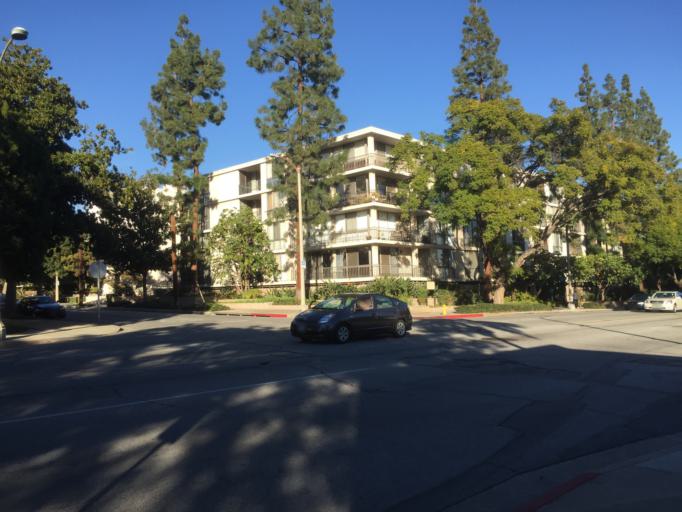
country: US
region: California
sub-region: Los Angeles County
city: Pasadena
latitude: 34.1403
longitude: -118.1386
